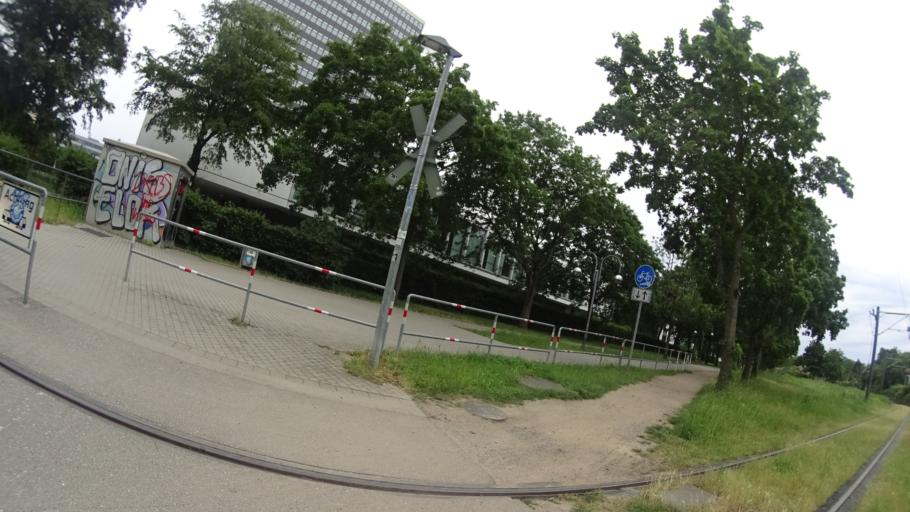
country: DE
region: Baden-Wuerttemberg
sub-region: Karlsruhe Region
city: Karlsruhe
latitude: 49.0047
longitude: 8.3782
